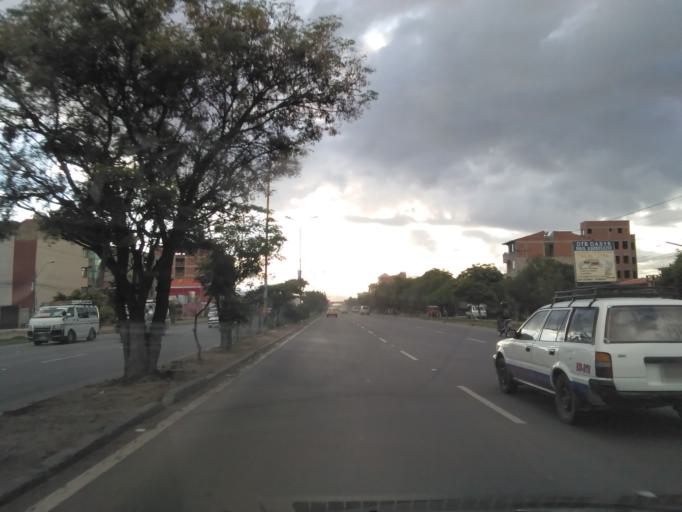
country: BO
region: Cochabamba
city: Cochabamba
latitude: -17.3921
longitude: -66.2127
